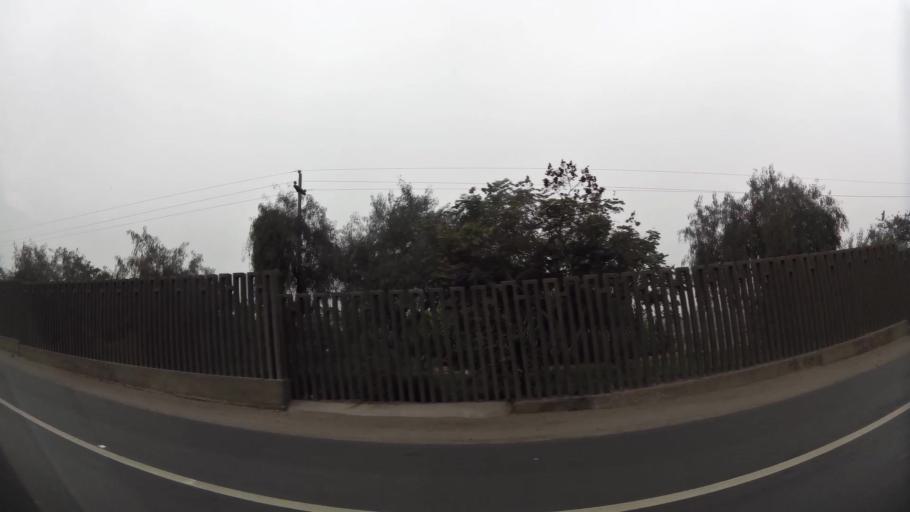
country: PE
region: Lima
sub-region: Lima
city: Vitarte
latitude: -12.0195
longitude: -76.9150
